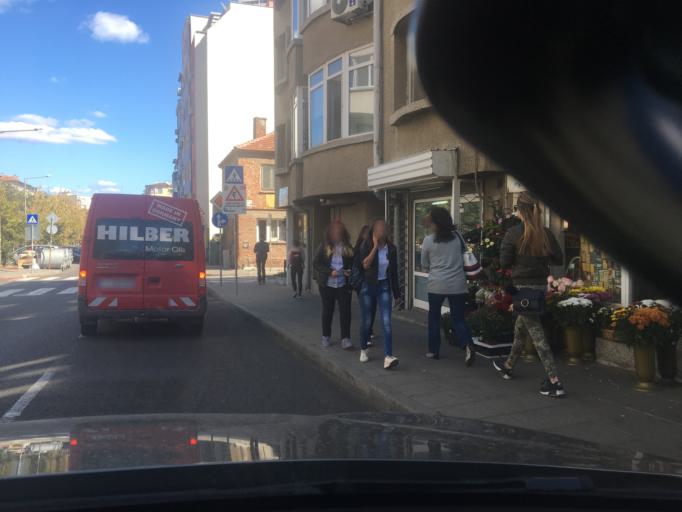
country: BG
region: Burgas
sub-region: Obshtina Burgas
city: Burgas
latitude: 42.5077
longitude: 27.4715
